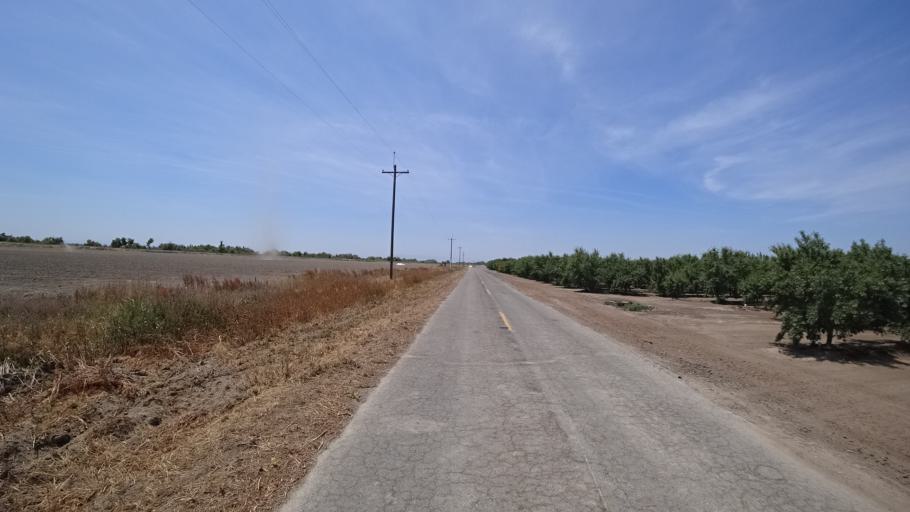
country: US
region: California
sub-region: Fresno County
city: Riverdale
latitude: 36.3875
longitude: -119.8933
